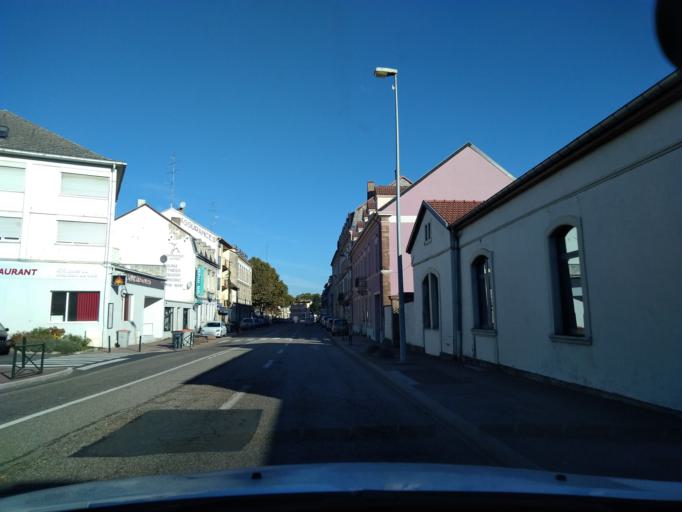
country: FR
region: Lorraine
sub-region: Departement de la Moselle
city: Sarreguemines
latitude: 49.1060
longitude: 7.0719
